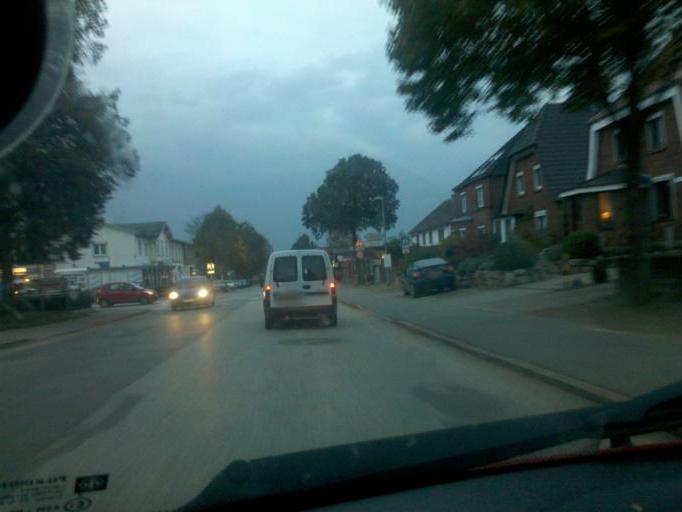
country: DE
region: Schleswig-Holstein
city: Ratekau
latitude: 53.9817
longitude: 10.7131
